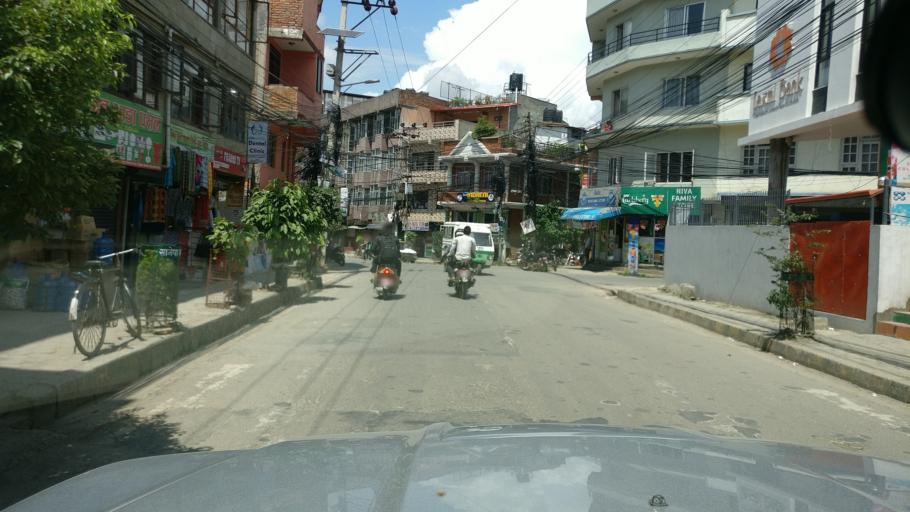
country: NP
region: Central Region
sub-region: Bagmati Zone
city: Patan
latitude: 27.6849
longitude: 85.3072
